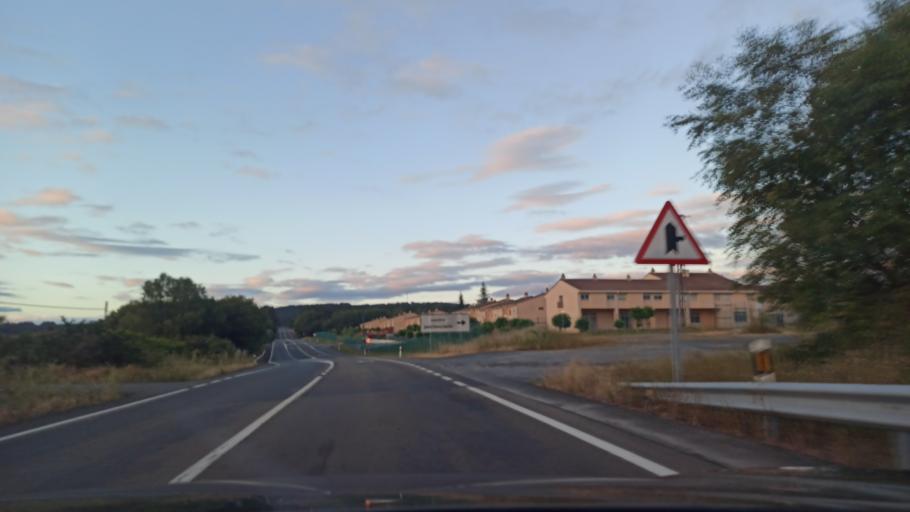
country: ES
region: Galicia
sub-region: Provincia de Lugo
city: Monterroso
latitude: 42.8092
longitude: -7.7739
